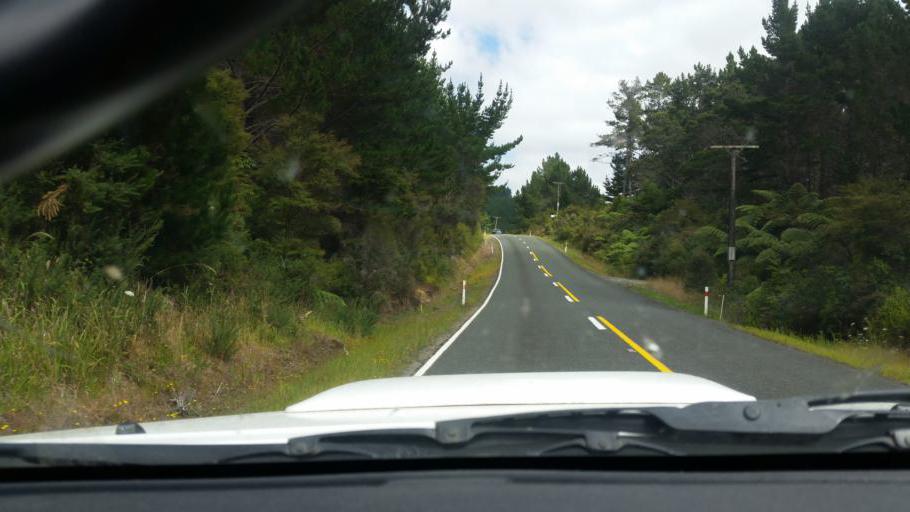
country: NZ
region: Northland
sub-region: Kaipara District
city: Dargaville
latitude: -35.8163
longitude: 173.7231
